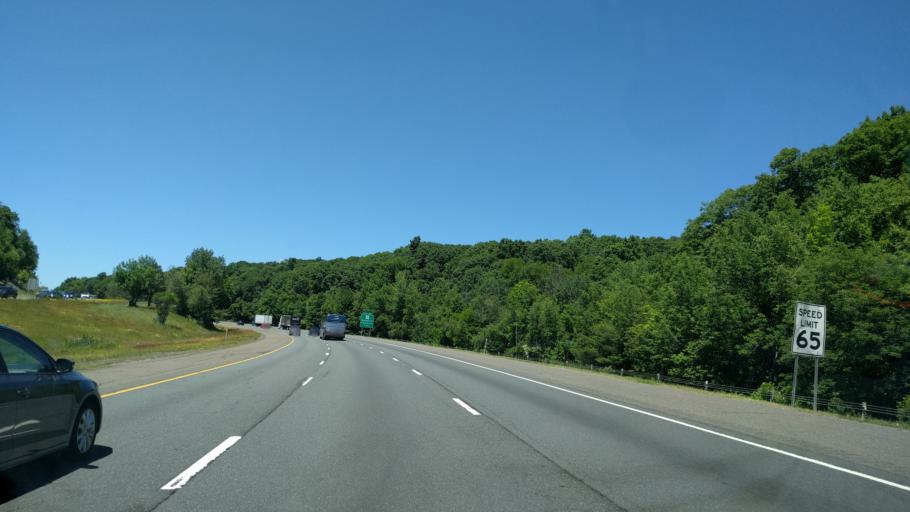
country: US
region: Connecticut
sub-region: Tolland County
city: Tolland
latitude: 41.8559
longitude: -72.3979
